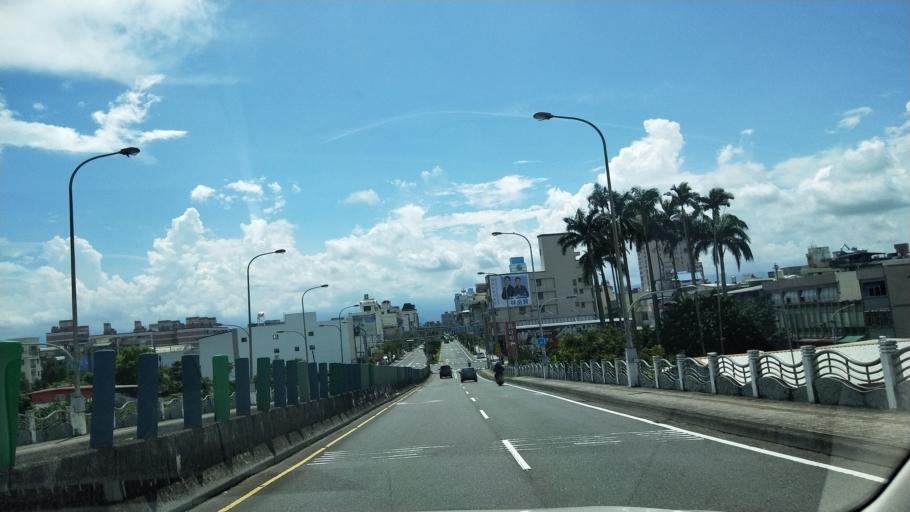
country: TW
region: Taiwan
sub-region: Yilan
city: Yilan
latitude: 24.7623
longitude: 121.7605
